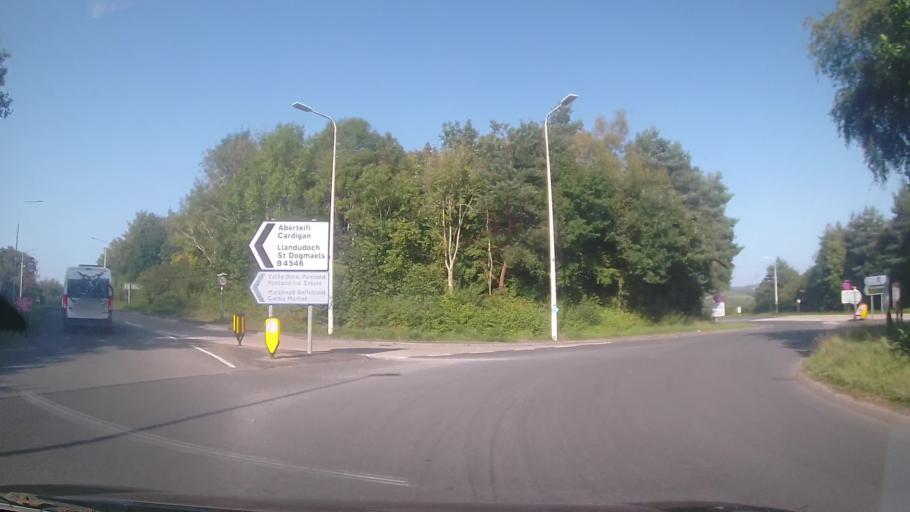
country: GB
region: Wales
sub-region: County of Ceredigion
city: Cardigan
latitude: 52.0761
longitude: -4.6564
